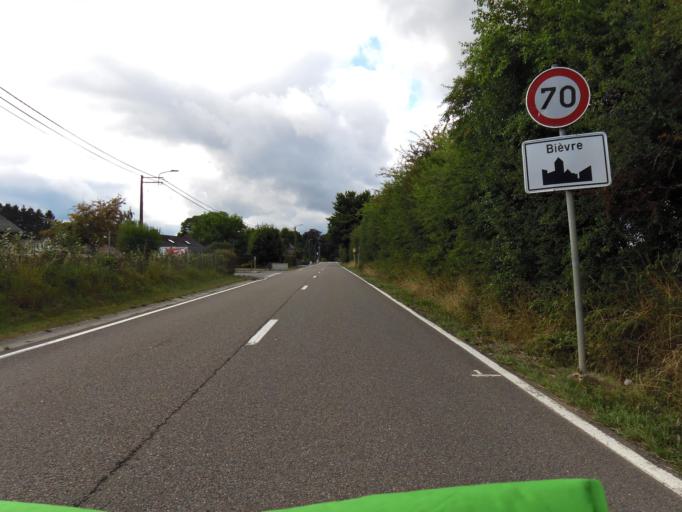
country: BE
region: Wallonia
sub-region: Province de Namur
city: Bievre
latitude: 49.9369
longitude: 5.0282
